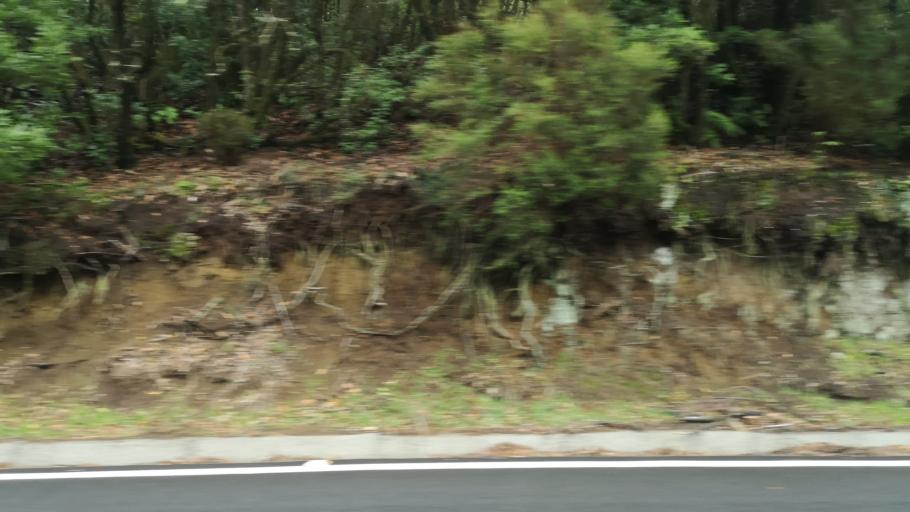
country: ES
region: Canary Islands
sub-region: Provincia de Santa Cruz de Tenerife
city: Vallehermosa
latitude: 28.1251
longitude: -17.2533
